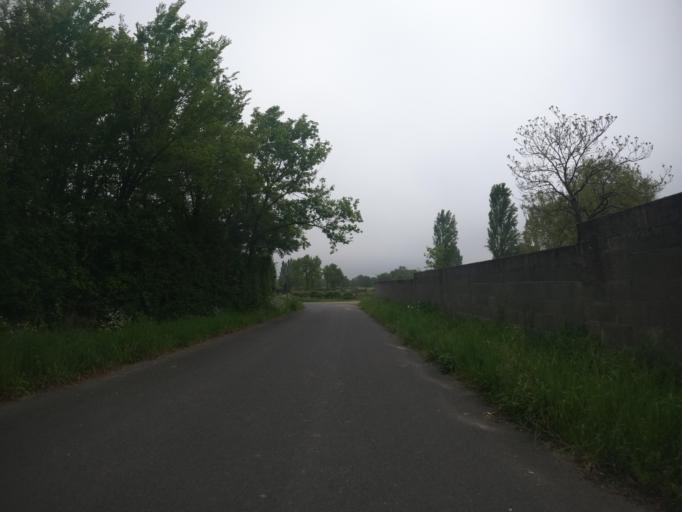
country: FR
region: Poitou-Charentes
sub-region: Departement des Deux-Sevres
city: Chiche
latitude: 46.8811
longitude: -0.3275
